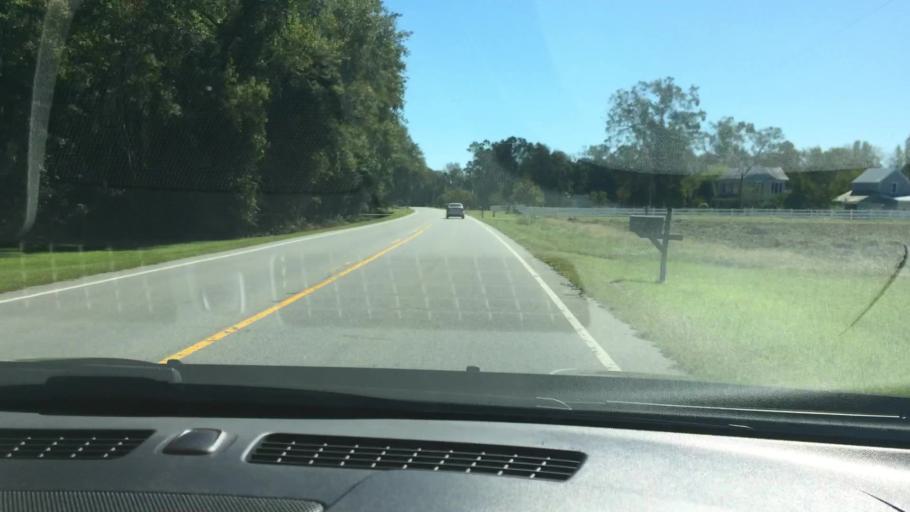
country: US
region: North Carolina
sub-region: Pitt County
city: Grifton
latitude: 35.3560
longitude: -77.3397
